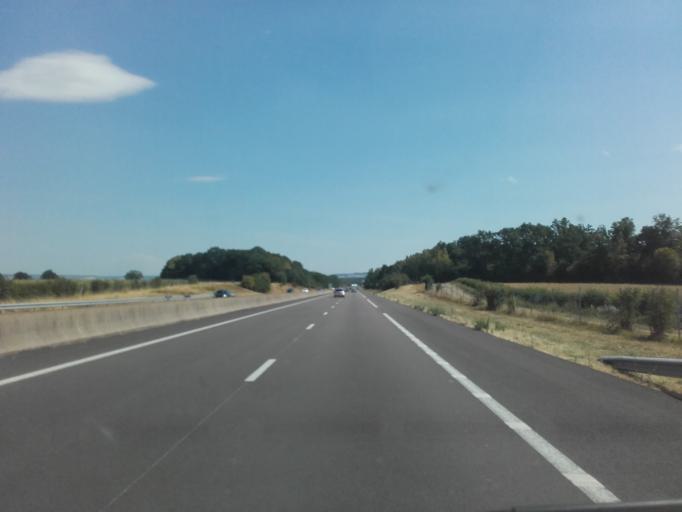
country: FR
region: Bourgogne
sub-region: Departement de la Cote-d'Or
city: Semur-en-Auxois
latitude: 47.4060
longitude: 4.3462
